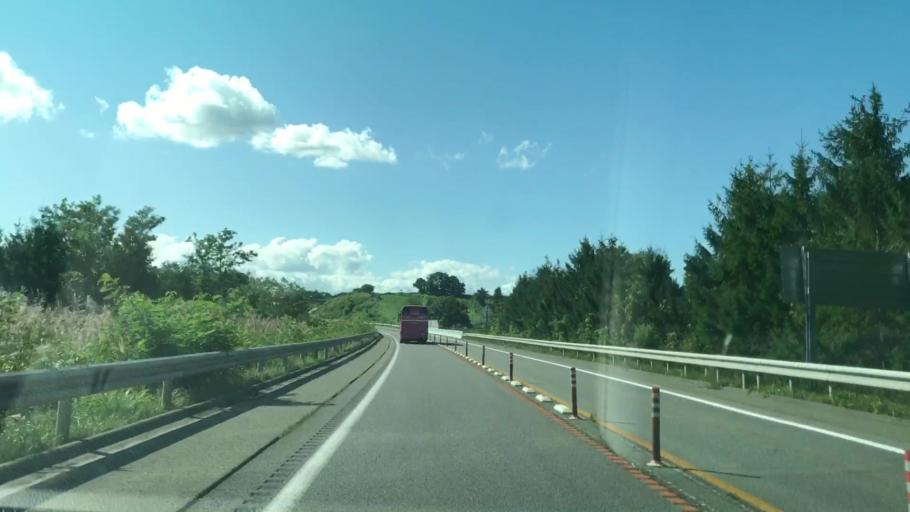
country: JP
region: Hokkaido
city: Date
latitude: 42.4954
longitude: 140.8715
